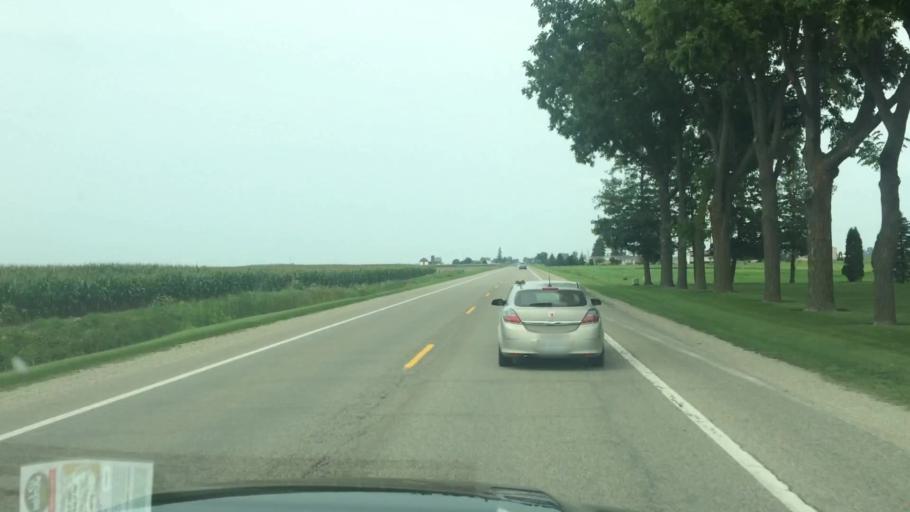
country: US
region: Michigan
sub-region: Huron County
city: Bad Axe
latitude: 43.9044
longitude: -83.0037
